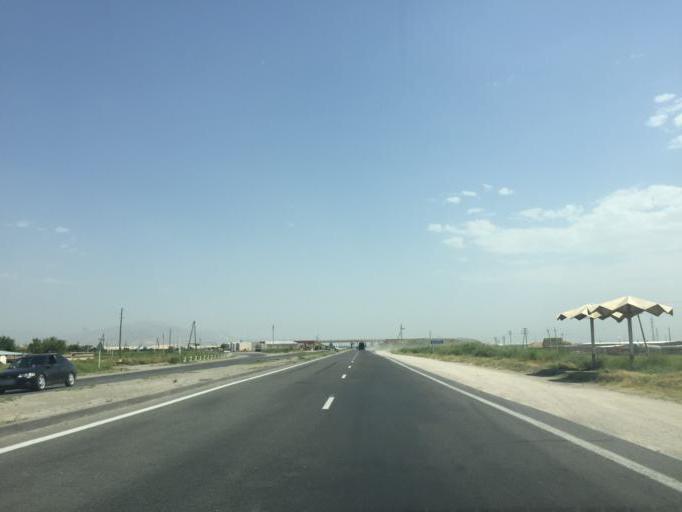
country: AM
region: Ararat
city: Shahumyan
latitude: 39.9355
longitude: 44.5632
